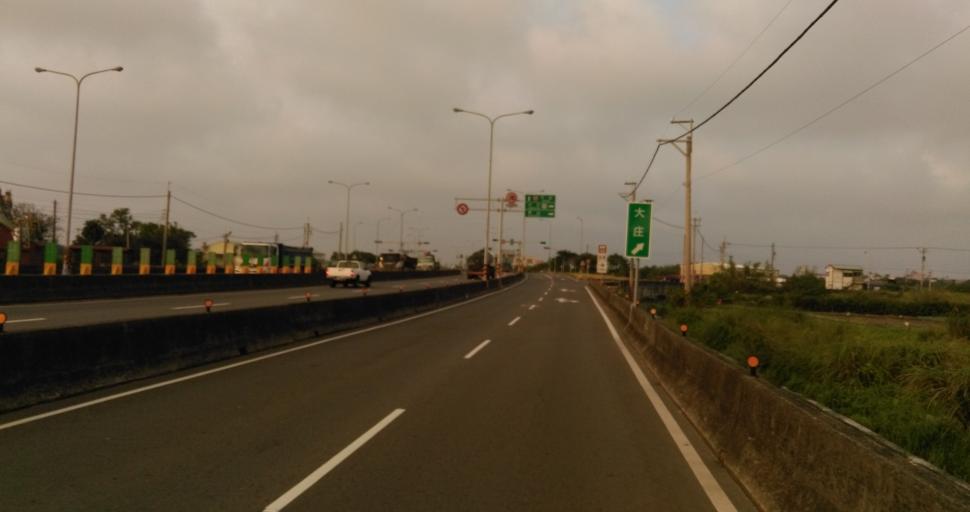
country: TW
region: Taiwan
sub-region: Hsinchu
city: Hsinchu
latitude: 24.7922
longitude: 120.9189
